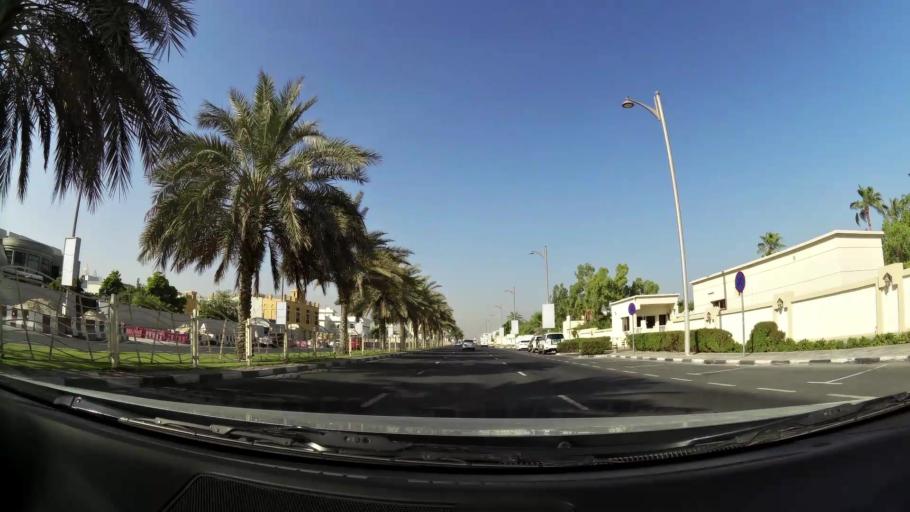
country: AE
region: Ash Shariqah
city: Sharjah
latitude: 25.2384
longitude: 55.2680
